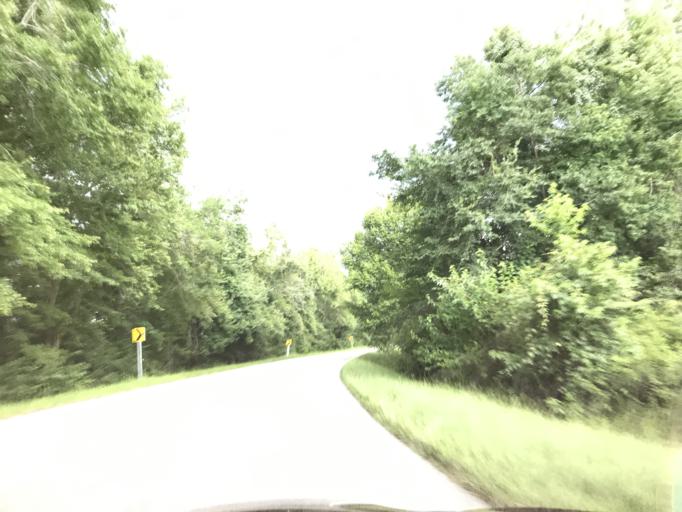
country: US
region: North Carolina
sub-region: Johnston County
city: Four Oaks
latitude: 35.5208
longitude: -78.4694
